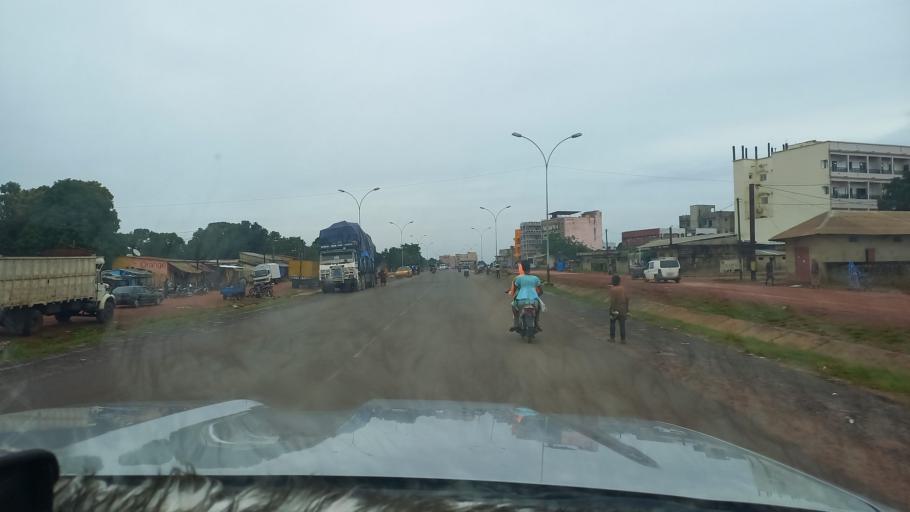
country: SN
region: Ziguinchor
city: Ziguinchor
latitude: 12.5530
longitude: -16.2665
